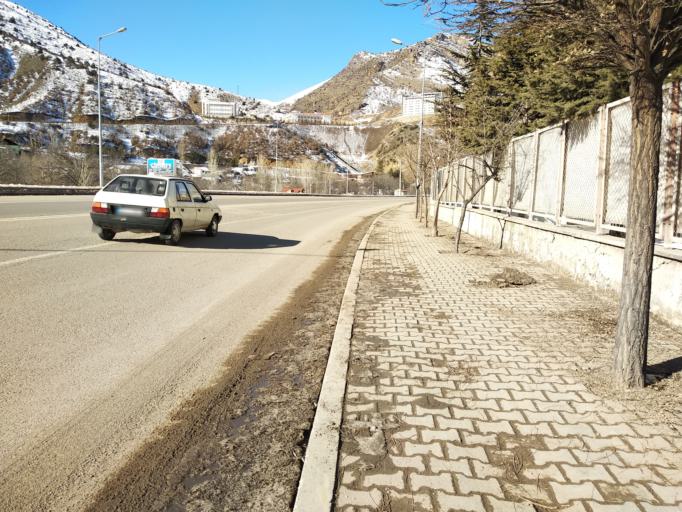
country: TR
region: Gumushane
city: Gumushkhane
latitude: 40.4370
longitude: 39.5074
